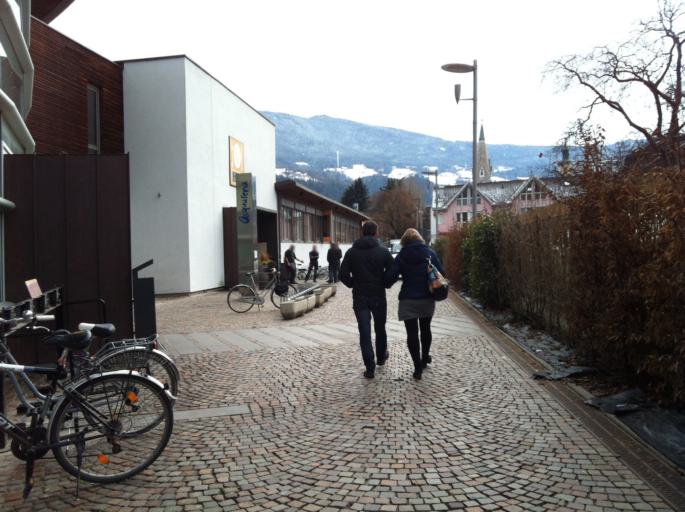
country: IT
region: Trentino-Alto Adige
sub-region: Bolzano
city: Bressanone
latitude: 46.7196
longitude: 11.6570
